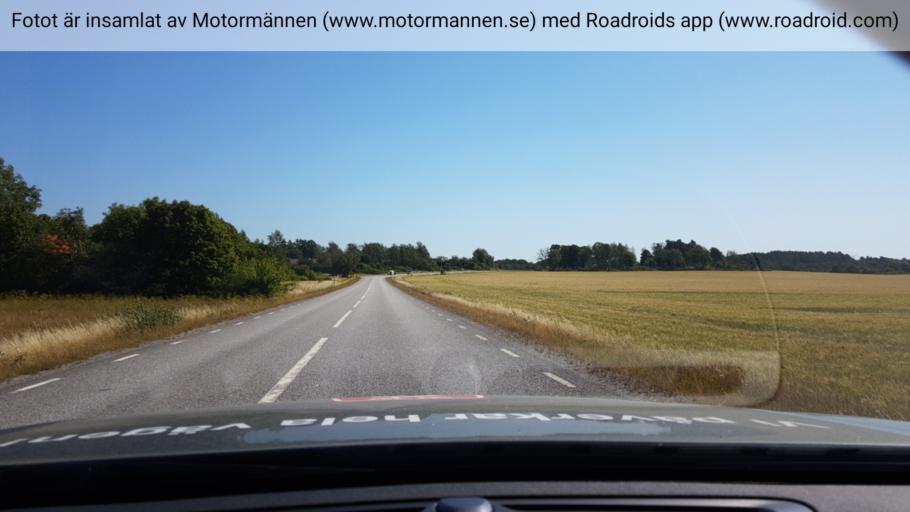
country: SE
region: Stockholm
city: Stenhamra
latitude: 59.3985
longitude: 17.5592
